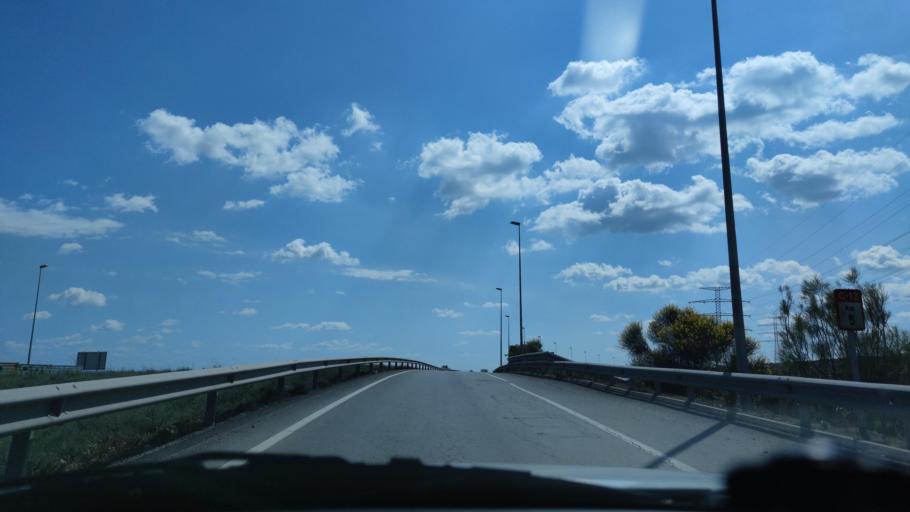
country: ES
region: Catalonia
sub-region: Provincia de Lleida
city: Alcoletge
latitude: 41.6054
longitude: 0.6721
